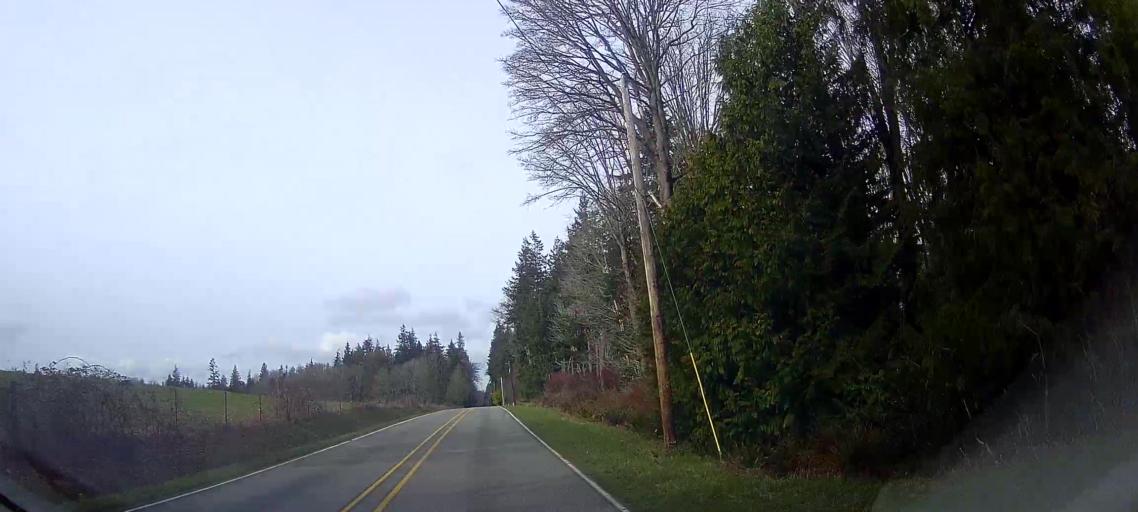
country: US
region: Washington
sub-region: Island County
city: Langley
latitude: 48.0905
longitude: -122.3914
